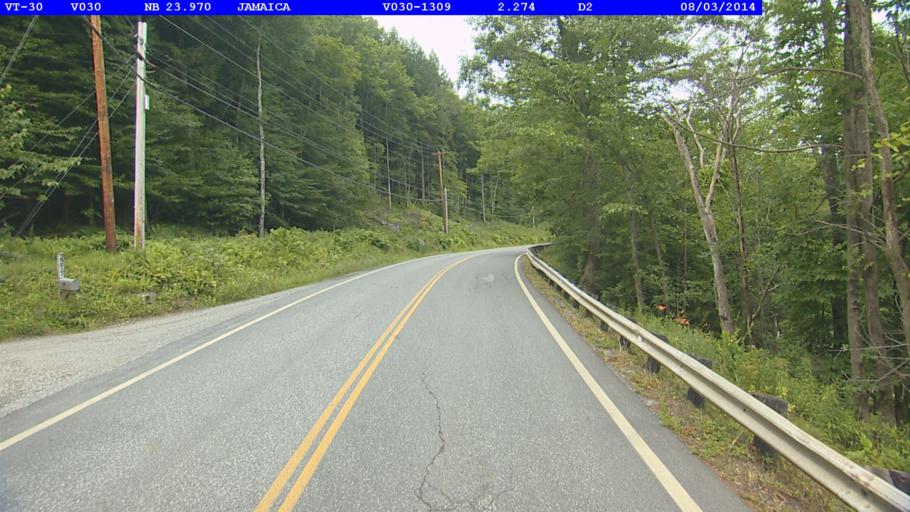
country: US
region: Vermont
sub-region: Windham County
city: Newfane
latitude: 43.0857
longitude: -72.7615
